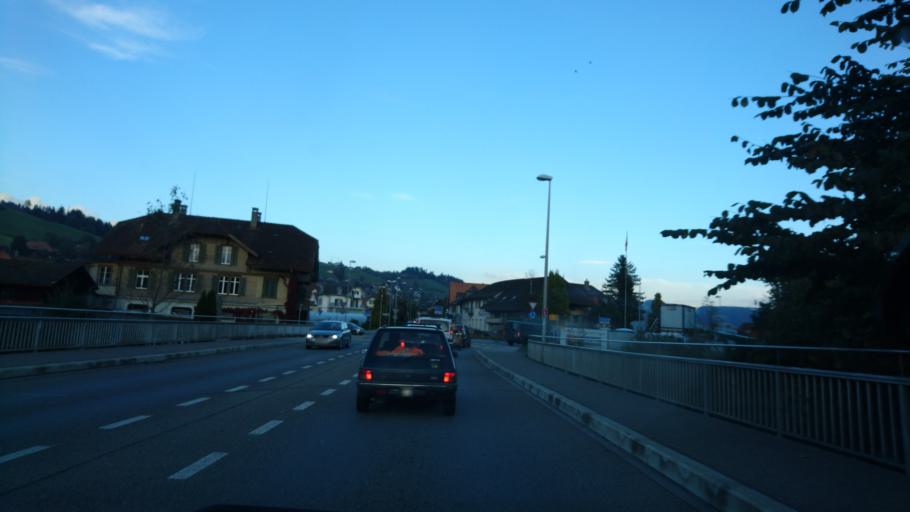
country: CH
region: Bern
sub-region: Emmental District
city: Langnau
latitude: 46.9394
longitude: 7.7782
